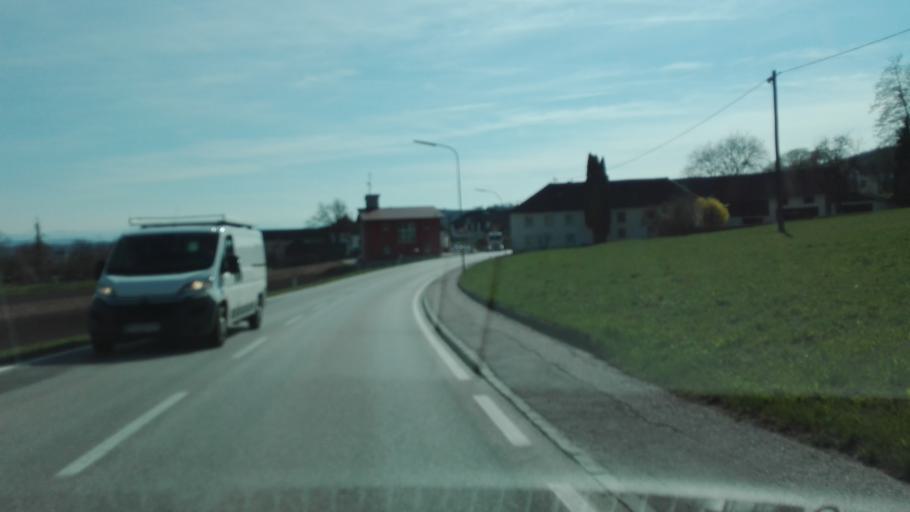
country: AT
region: Lower Austria
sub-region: Politischer Bezirk Amstetten
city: Ennsdorf
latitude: 48.2599
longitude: 14.5419
